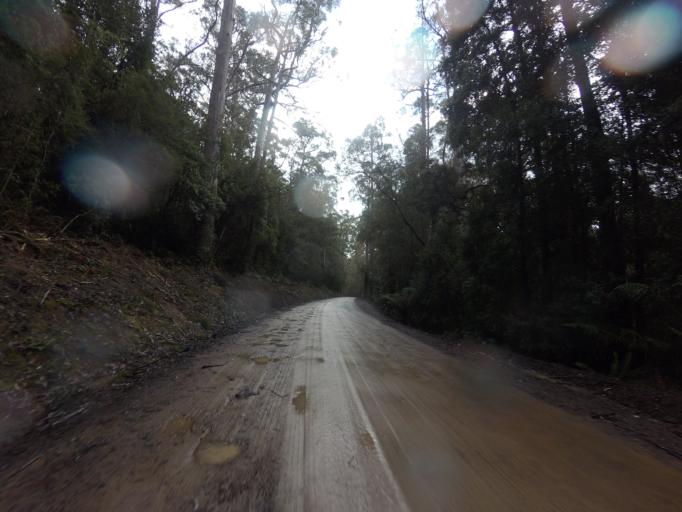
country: AU
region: Tasmania
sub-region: Huon Valley
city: Geeveston
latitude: -43.5738
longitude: 146.8883
